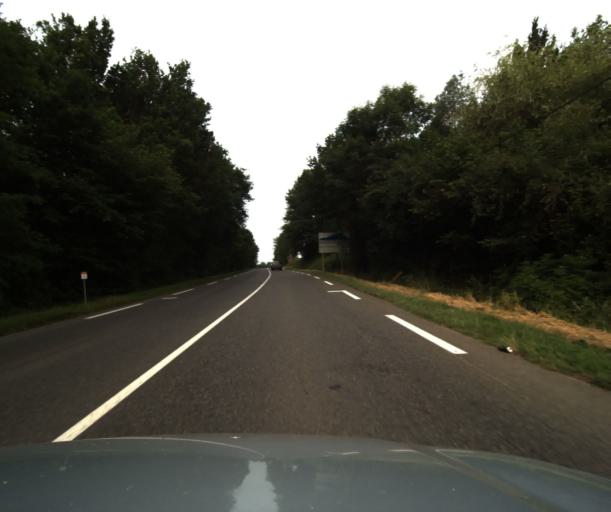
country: FR
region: Midi-Pyrenees
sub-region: Departement des Hautes-Pyrenees
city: Rabastens-de-Bigorre
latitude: 43.3921
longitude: 0.1646
